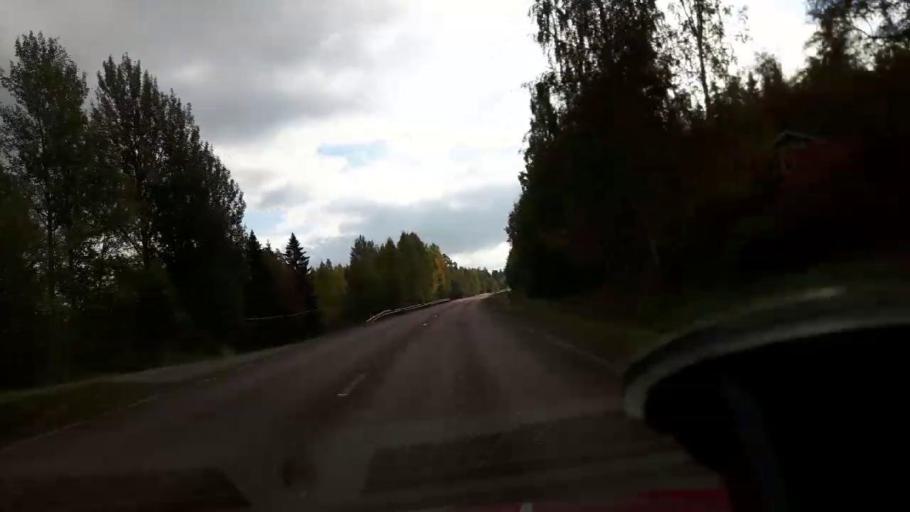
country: SE
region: Gaevleborg
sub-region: Bollnas Kommun
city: Arbra
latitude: 61.5905
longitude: 16.3065
